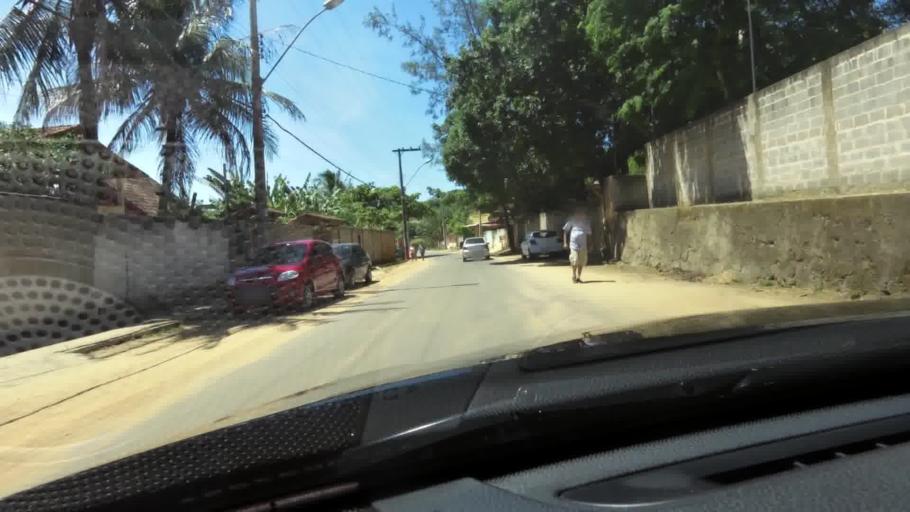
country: BR
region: Espirito Santo
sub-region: Guarapari
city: Guarapari
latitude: -20.6214
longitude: -40.4675
